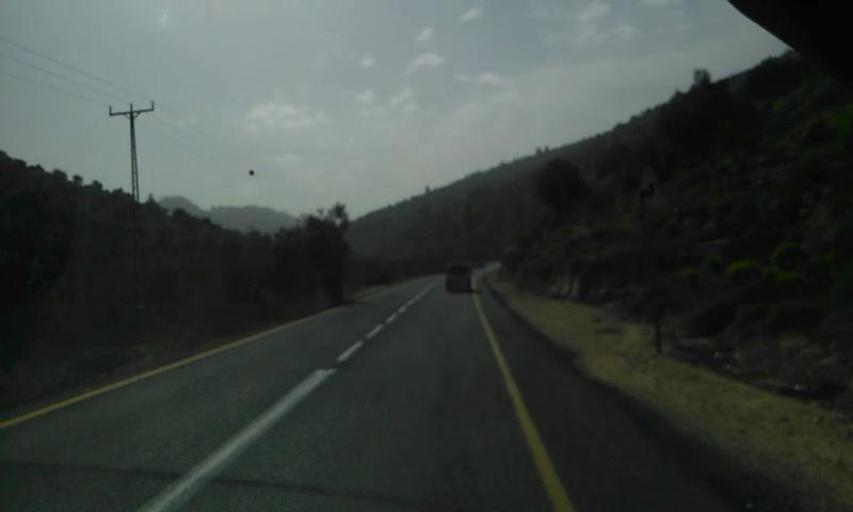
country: PS
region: West Bank
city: Silwad
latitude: 31.9968
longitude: 35.2402
